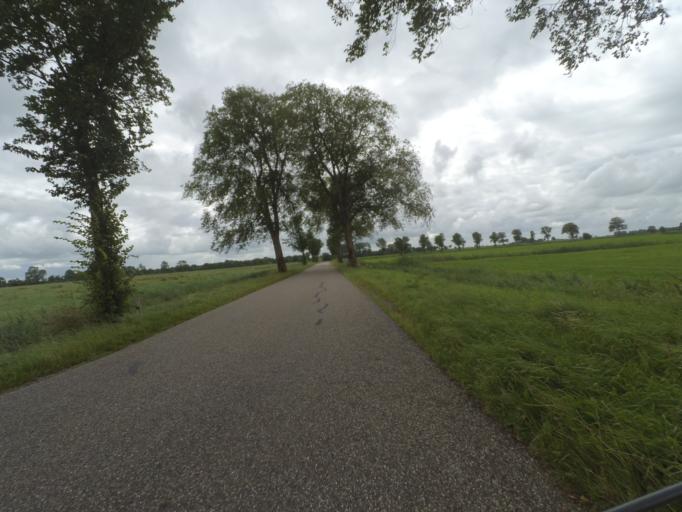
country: NL
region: Friesland
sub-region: Gemeente Kollumerland en Nieuwkruisland
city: Kollumerzwaag
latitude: 53.3004
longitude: 6.0871
